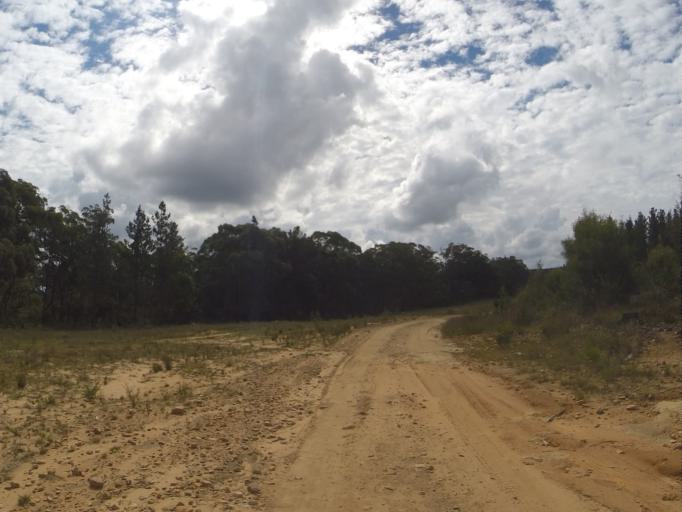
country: AU
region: New South Wales
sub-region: Wingecarribee
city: Moss Vale
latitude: -34.5207
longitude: 150.2252
